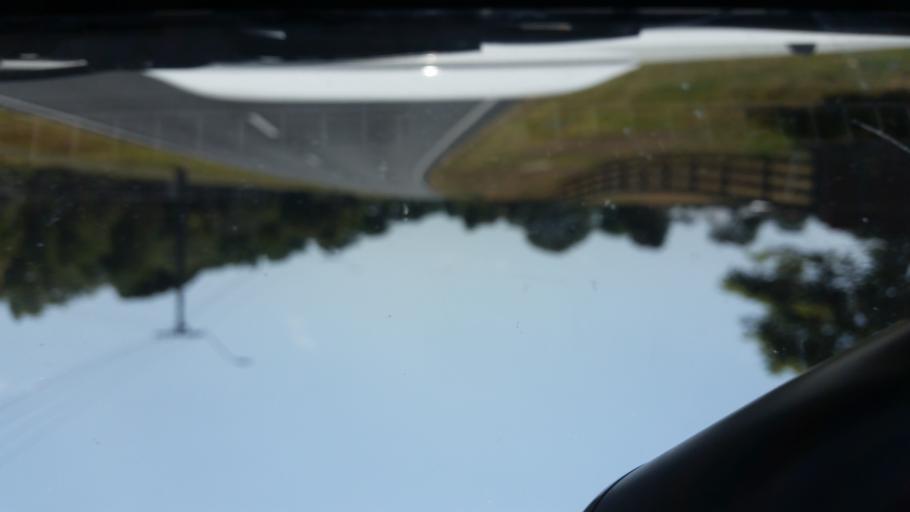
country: NZ
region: Northland
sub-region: Kaipara District
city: Dargaville
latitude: -36.0271
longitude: 173.9177
